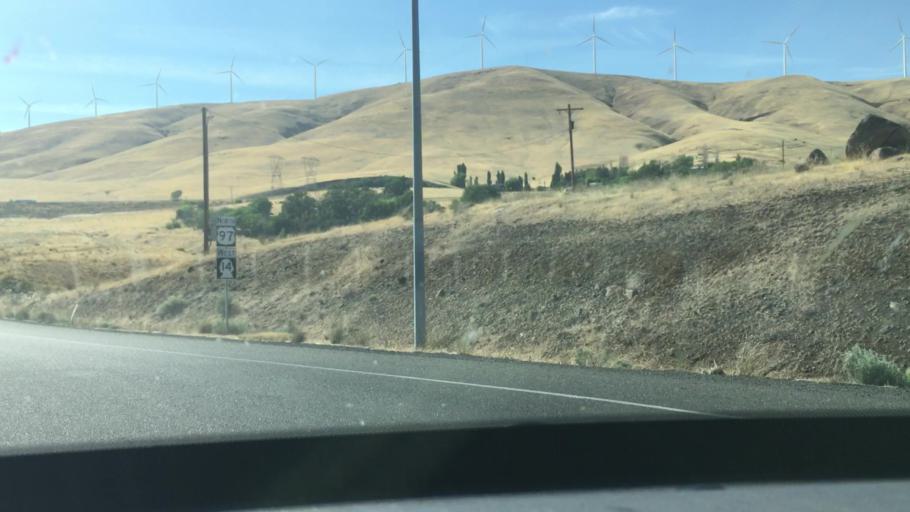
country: US
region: Washington
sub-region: Klickitat County
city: Goldendale
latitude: 45.6979
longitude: -120.8155
